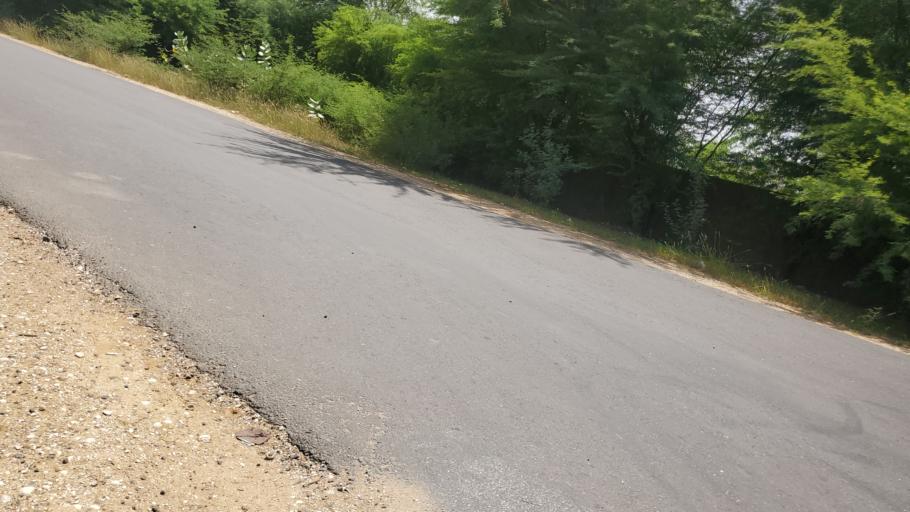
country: SN
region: Saint-Louis
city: Saint-Louis
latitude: 16.0579
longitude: -16.4276
